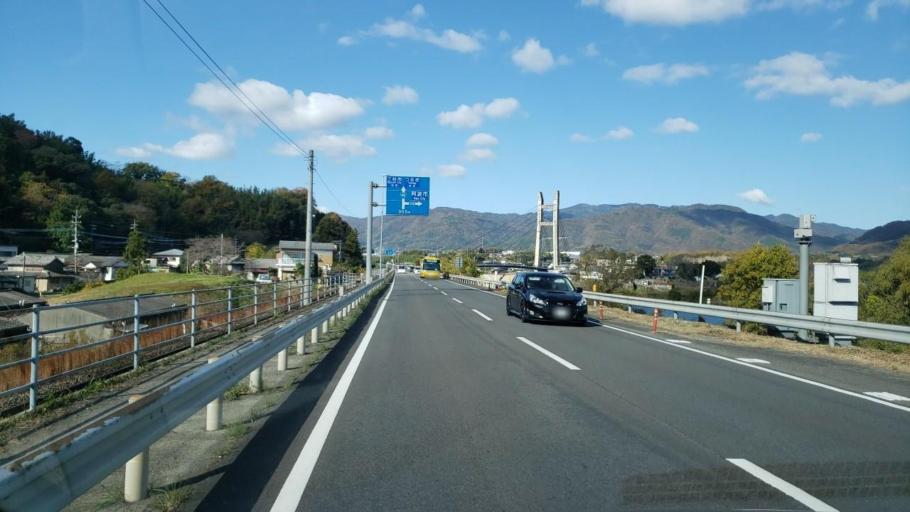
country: JP
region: Tokushima
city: Wakimachi
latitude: 34.0628
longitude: 134.1983
